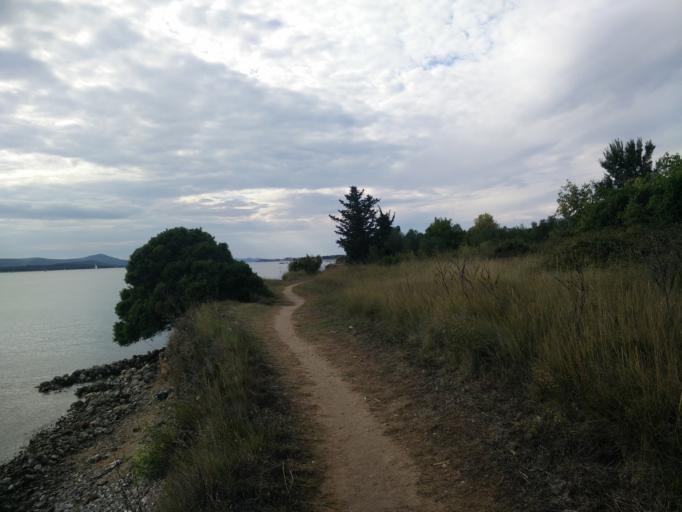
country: HR
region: Zadarska
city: Biograd na Moru
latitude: 43.9497
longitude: 15.4413
